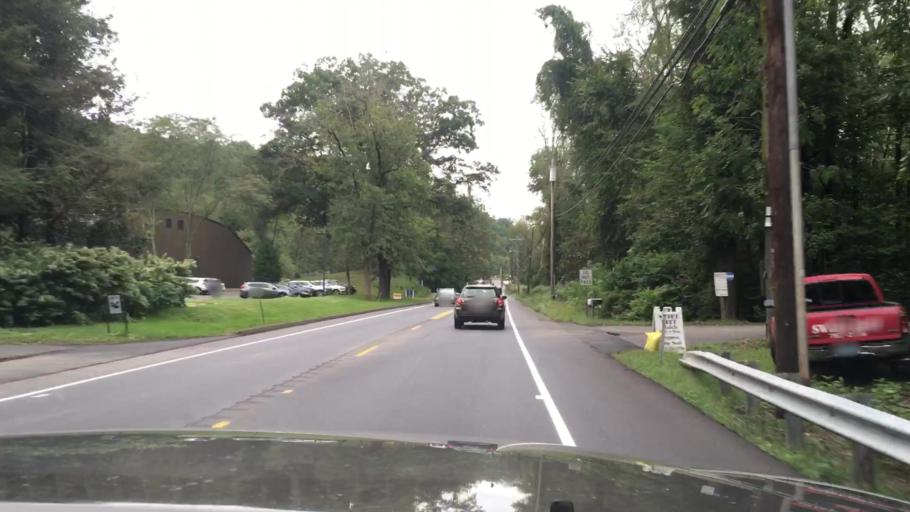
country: US
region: Connecticut
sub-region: Fairfield County
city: Georgetown
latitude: 41.2344
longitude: -73.4292
